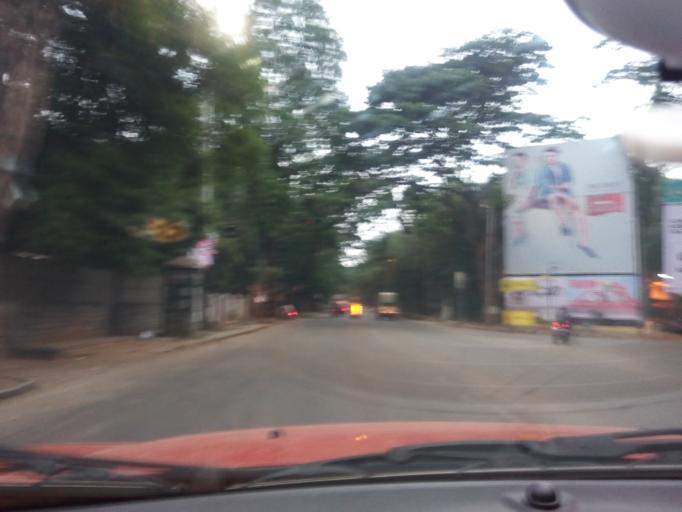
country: IN
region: Karnataka
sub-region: Bangalore Urban
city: Bangalore
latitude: 13.0148
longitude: 77.5731
